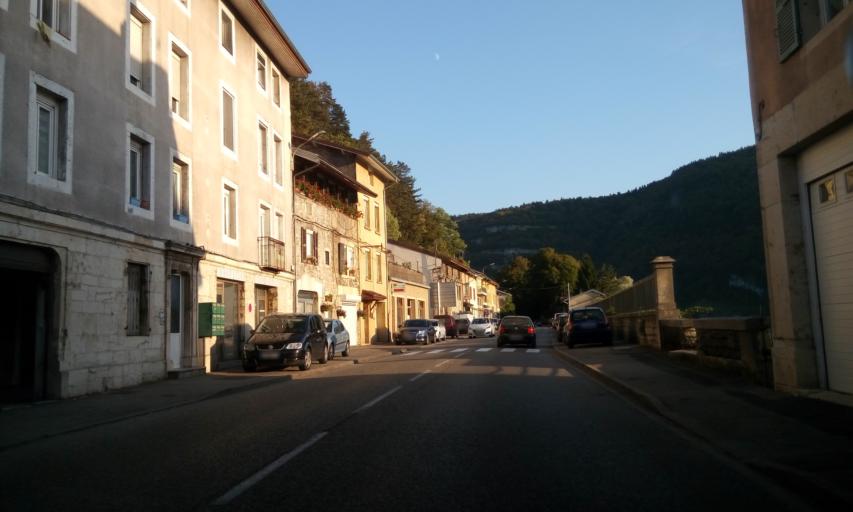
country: FR
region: Rhone-Alpes
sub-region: Departement de l'Ain
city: Montreal-la-Cluse
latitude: 46.1699
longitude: 5.5773
